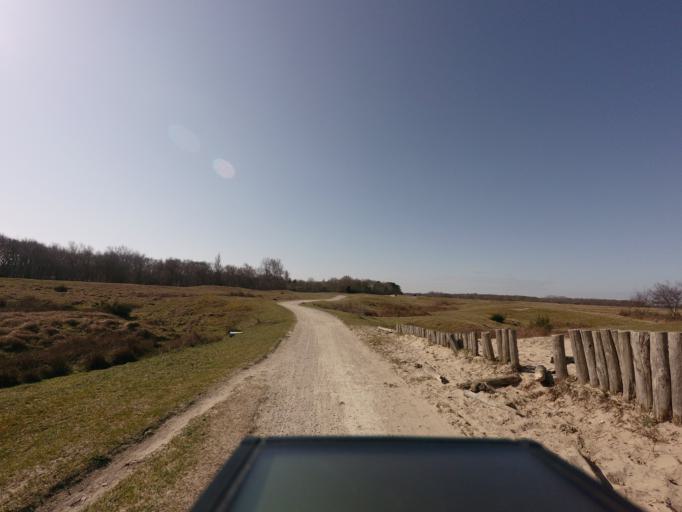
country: NL
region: Zeeland
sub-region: Schouwen-Duiveland
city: Renesse
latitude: 51.7196
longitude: 3.7571
